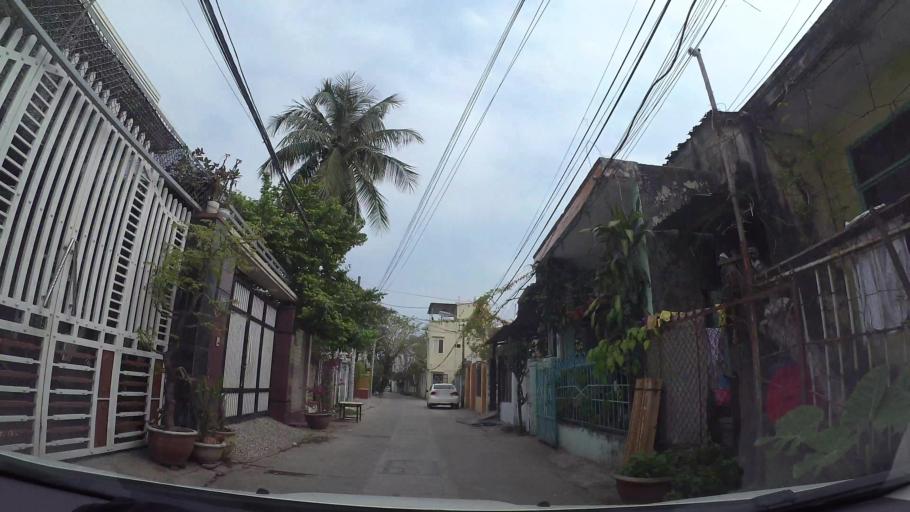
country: VN
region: Da Nang
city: Son Tra
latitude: 16.0943
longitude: 108.2455
